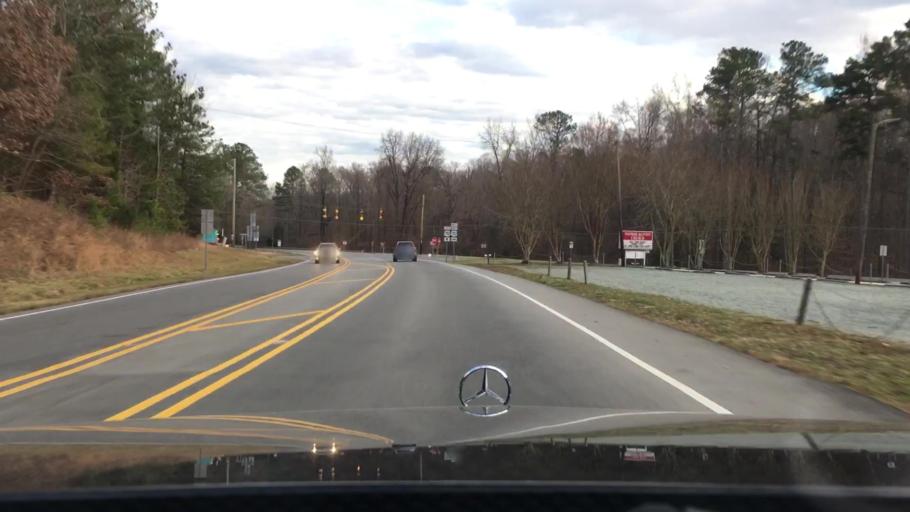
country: US
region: North Carolina
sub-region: Orange County
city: Hillsborough
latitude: 36.0570
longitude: -79.0506
